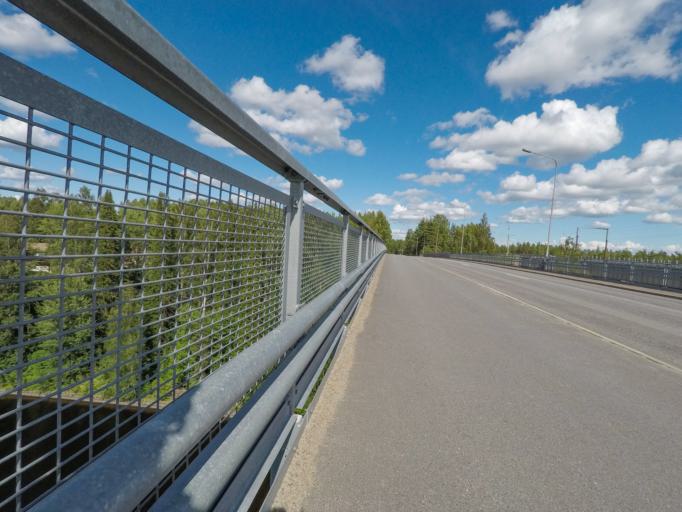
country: FI
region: South Karelia
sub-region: Lappeenranta
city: Lappeenranta
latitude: 61.0780
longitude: 28.2916
